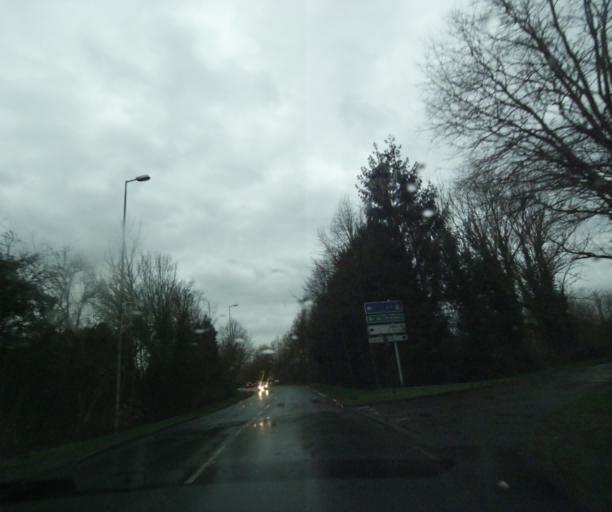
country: FR
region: Nord-Pas-de-Calais
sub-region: Departement du Nord
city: Conde-sur-l'Escaut
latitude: 50.4450
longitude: 3.5945
